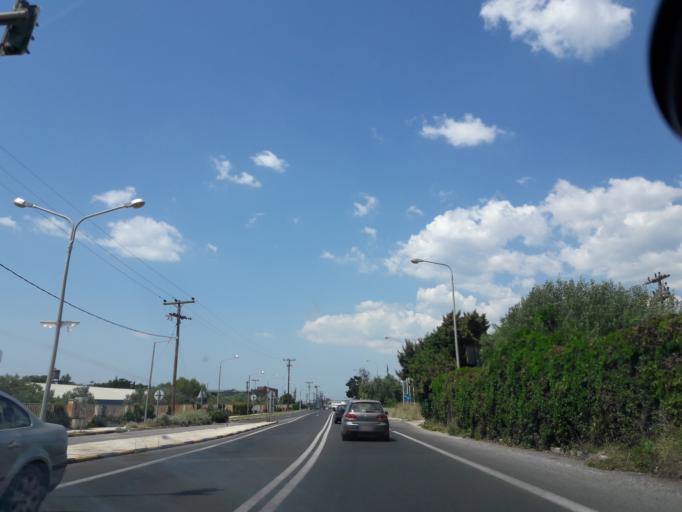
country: GR
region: Central Macedonia
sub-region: Nomos Thessalonikis
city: Thermi
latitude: 40.5388
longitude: 23.0340
